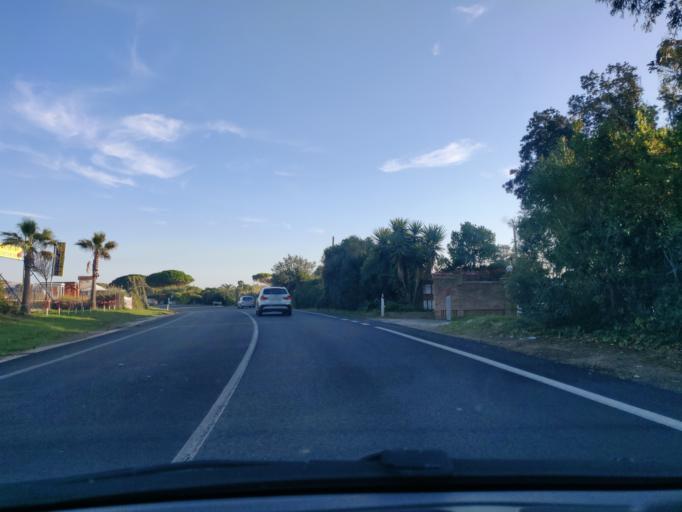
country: IT
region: Latium
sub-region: Citta metropolitana di Roma Capitale
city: Civitavecchia
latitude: 42.0489
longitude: 11.8209
